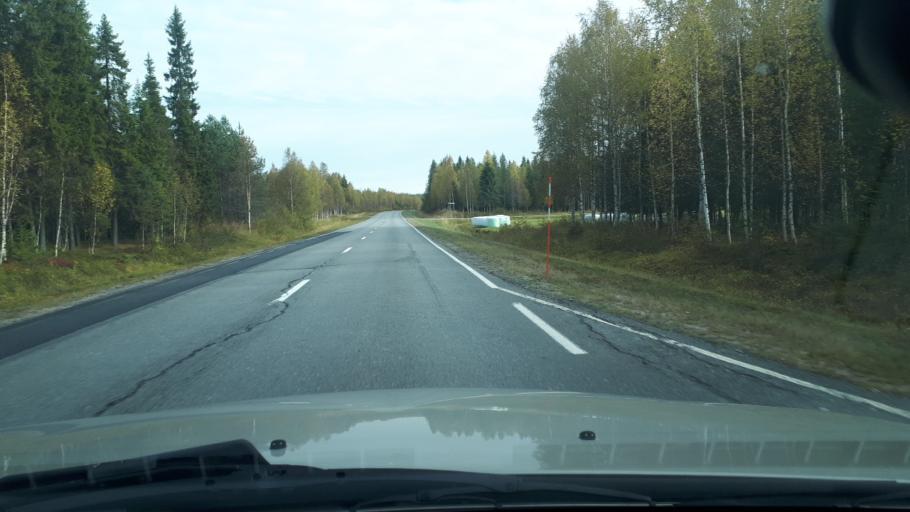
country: FI
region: Lapland
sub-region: Rovaniemi
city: Ranua
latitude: 65.9762
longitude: 26.1182
